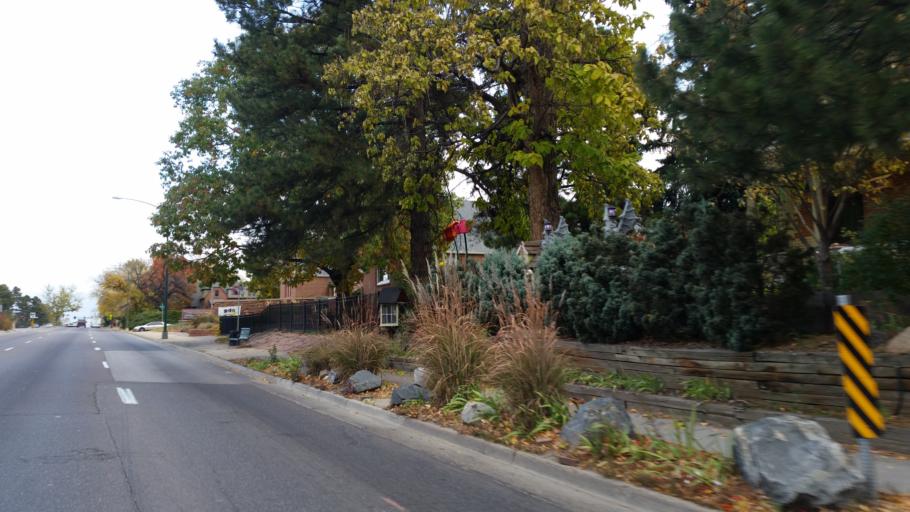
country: US
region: Colorado
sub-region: Arapahoe County
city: Glendale
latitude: 39.7440
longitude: -104.9406
